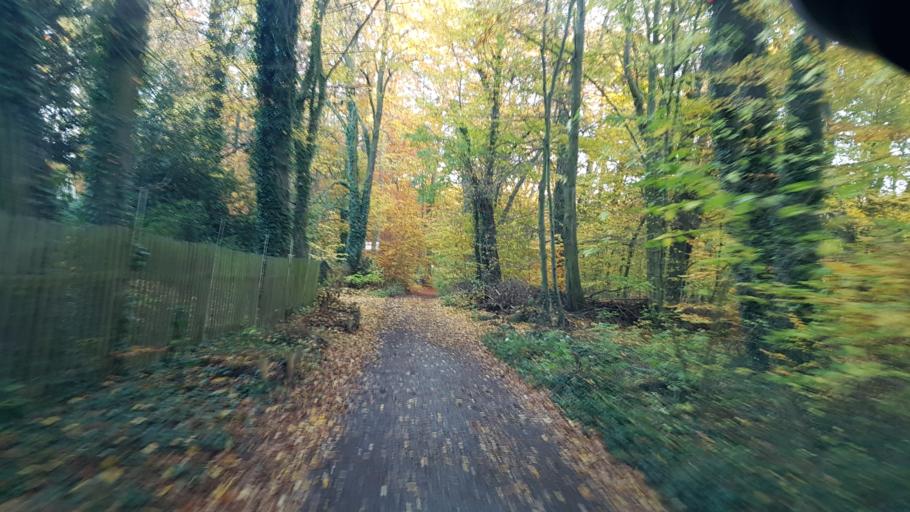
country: DE
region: Saxony
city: Schildau
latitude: 51.4254
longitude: 12.9743
